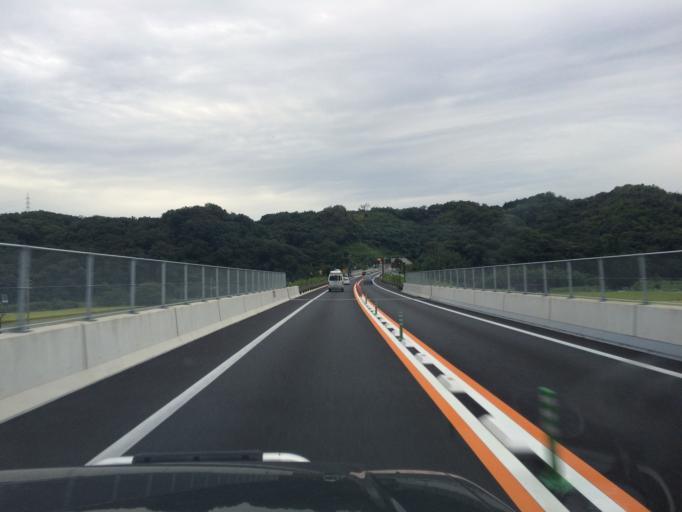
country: JP
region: Tottori
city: Tottori
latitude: 35.4938
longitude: 134.1903
